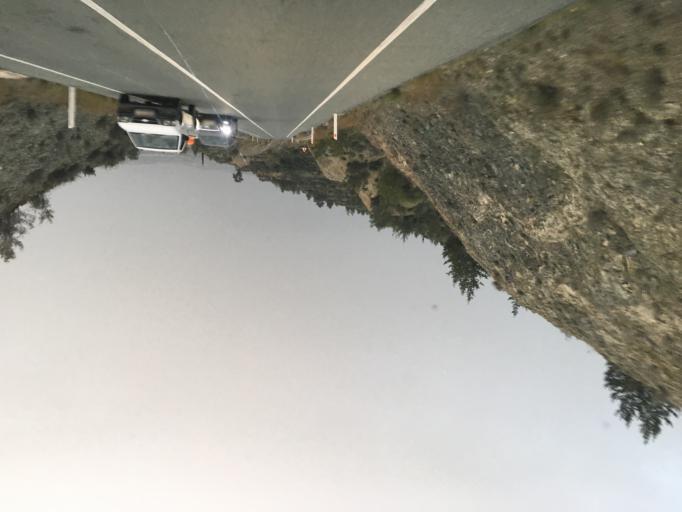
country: CY
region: Limassol
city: Parekklisha
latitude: 34.7926
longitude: 33.1581
